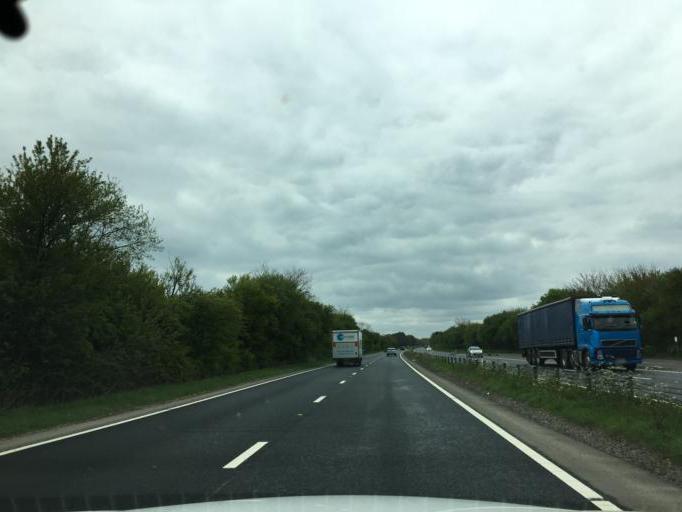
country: GB
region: Wales
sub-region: Carmarthenshire
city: Llangynog
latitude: 51.8389
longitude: -4.4209
